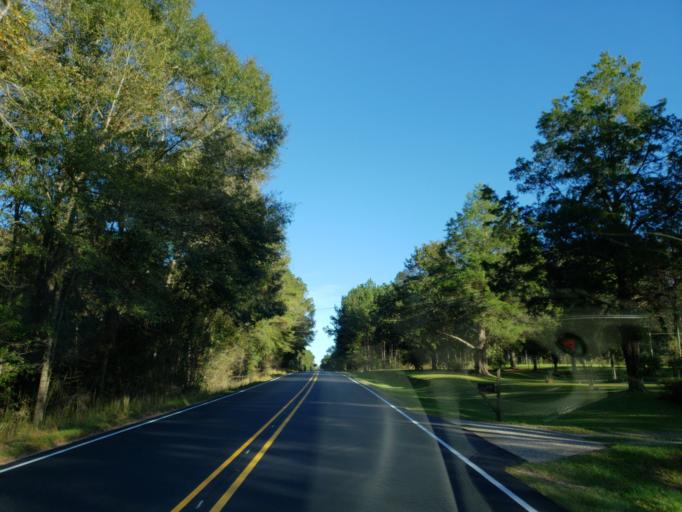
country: US
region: Mississippi
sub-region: Perry County
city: Richton
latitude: 31.3617
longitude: -88.8021
